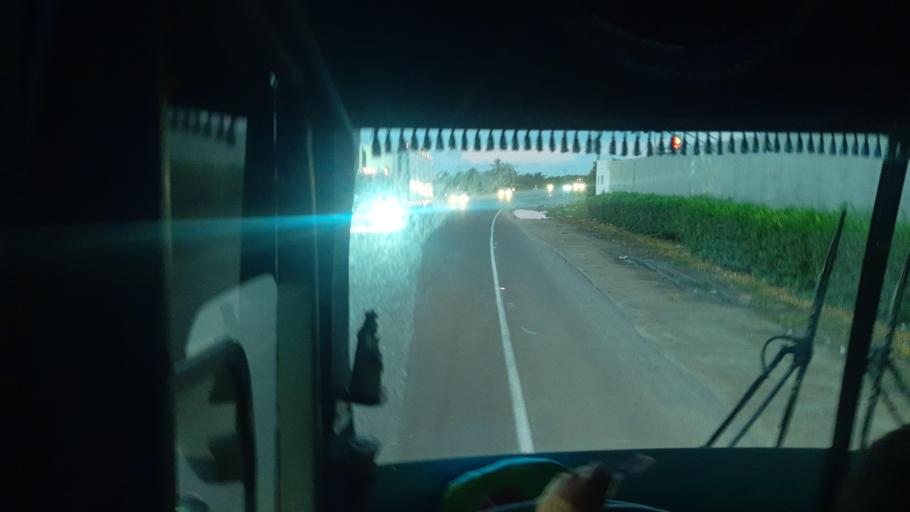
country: CO
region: Atlantico
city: Barranquilla
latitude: 10.9583
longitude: -74.7449
